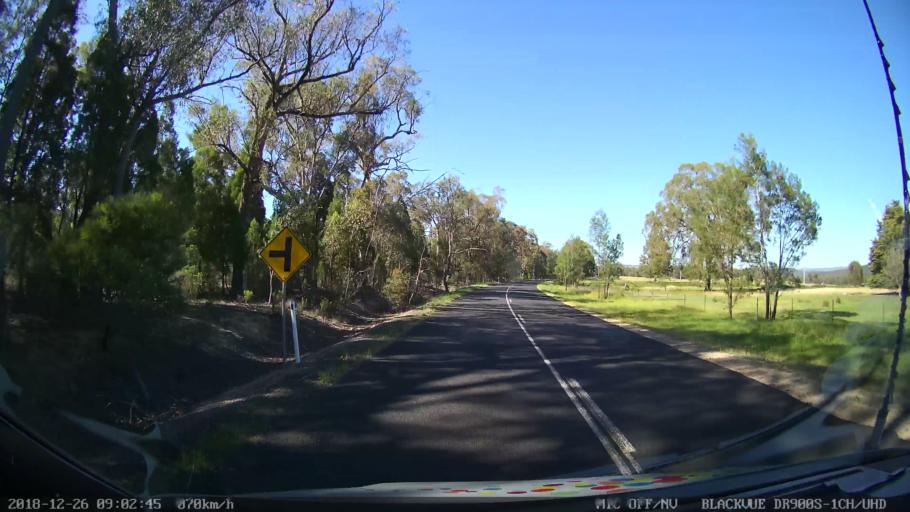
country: AU
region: New South Wales
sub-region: Mid-Western Regional
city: Kandos
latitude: -32.6560
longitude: 150.0176
